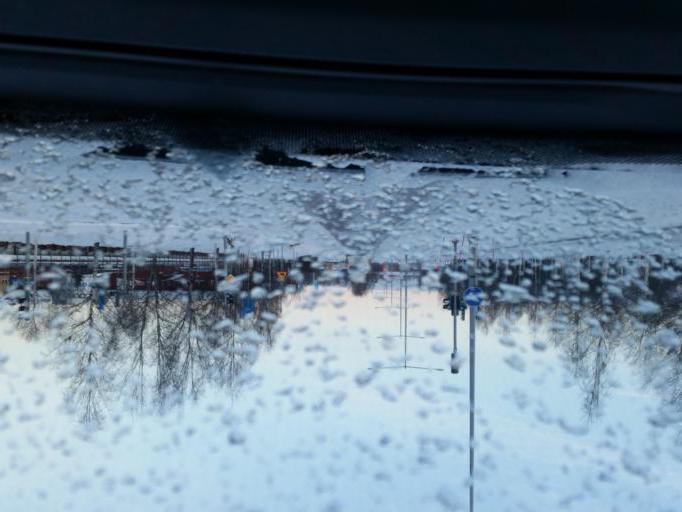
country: SE
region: Norrbotten
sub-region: Pitea Kommun
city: Pitea
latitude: 65.3152
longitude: 21.4769
